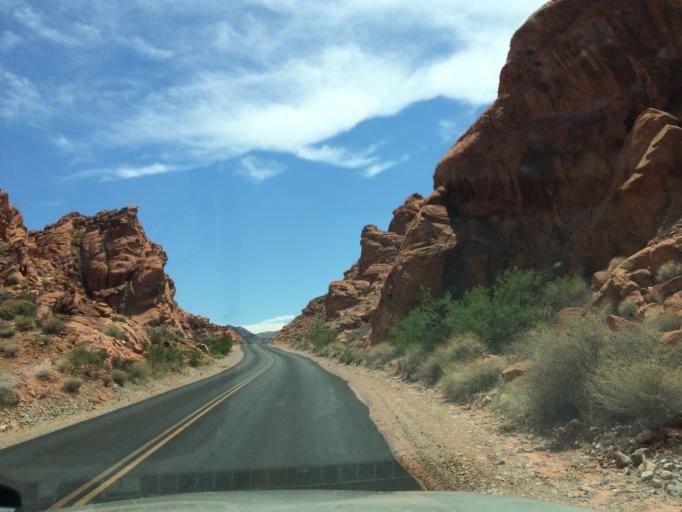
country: US
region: Nevada
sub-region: Clark County
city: Moapa Valley
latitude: 36.4350
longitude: -114.5175
